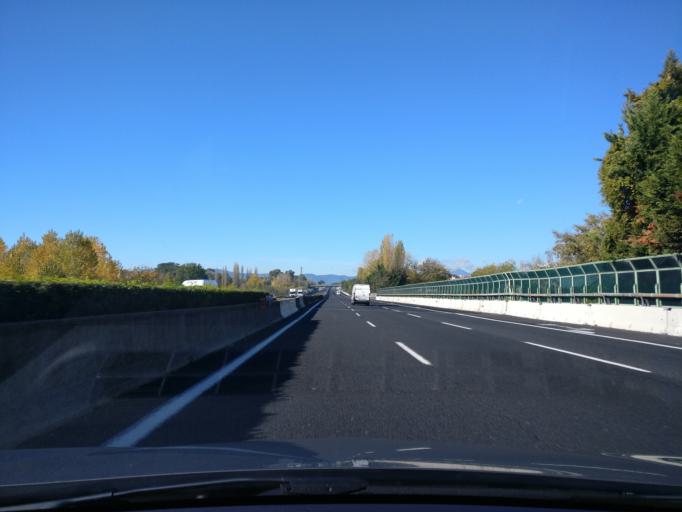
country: IT
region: Latium
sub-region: Provincia di Frosinone
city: Ceprano
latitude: 41.5431
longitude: 13.5194
